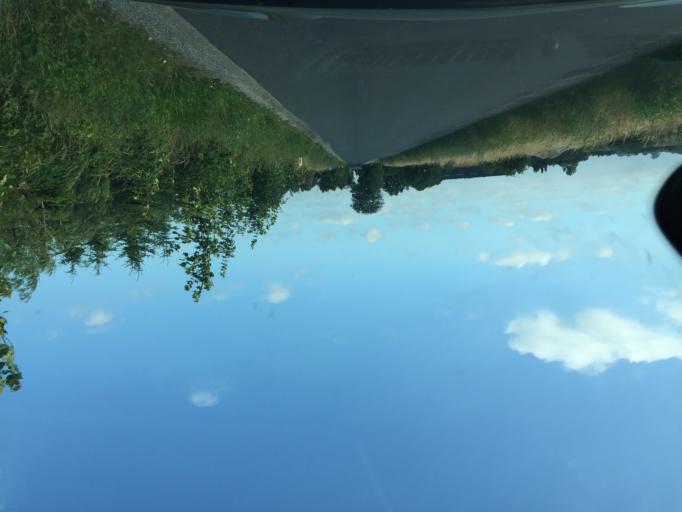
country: DK
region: South Denmark
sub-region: Kerteminde Kommune
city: Langeskov
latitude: 55.3246
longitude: 10.5425
